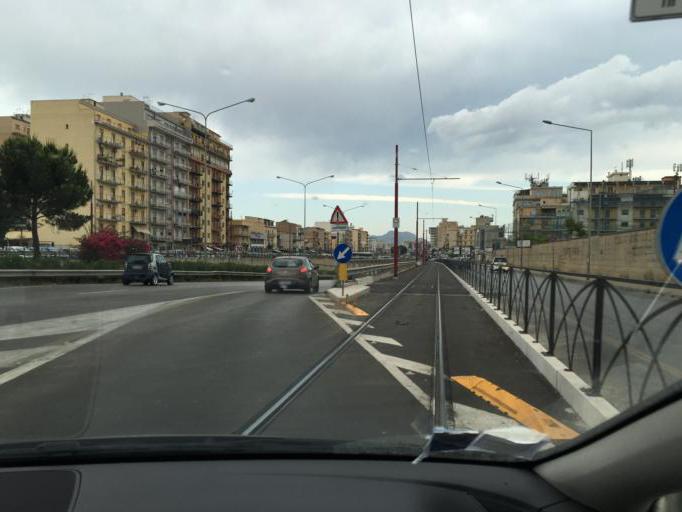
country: IT
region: Sicily
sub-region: Palermo
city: Palermo
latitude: 38.1084
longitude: 13.3303
